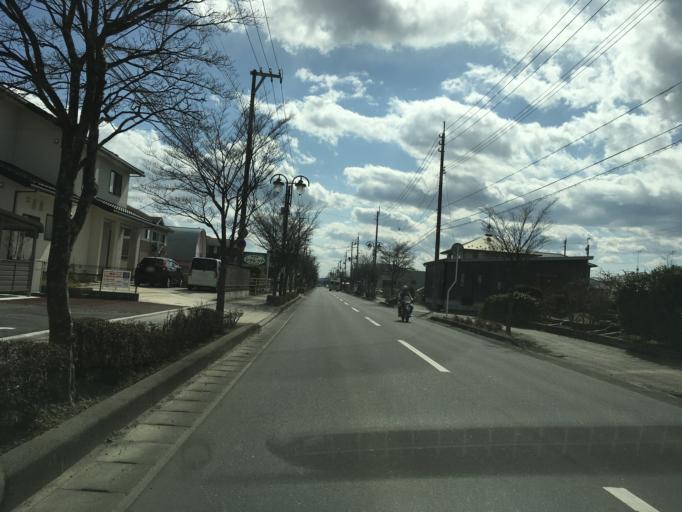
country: JP
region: Miyagi
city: Wakuya
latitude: 38.7055
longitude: 141.2149
